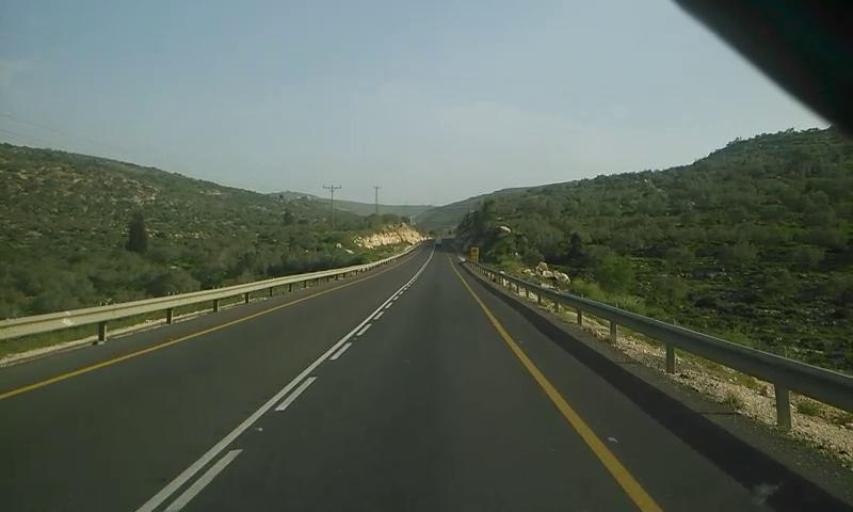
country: PS
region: West Bank
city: Jit
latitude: 32.2230
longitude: 35.1740
